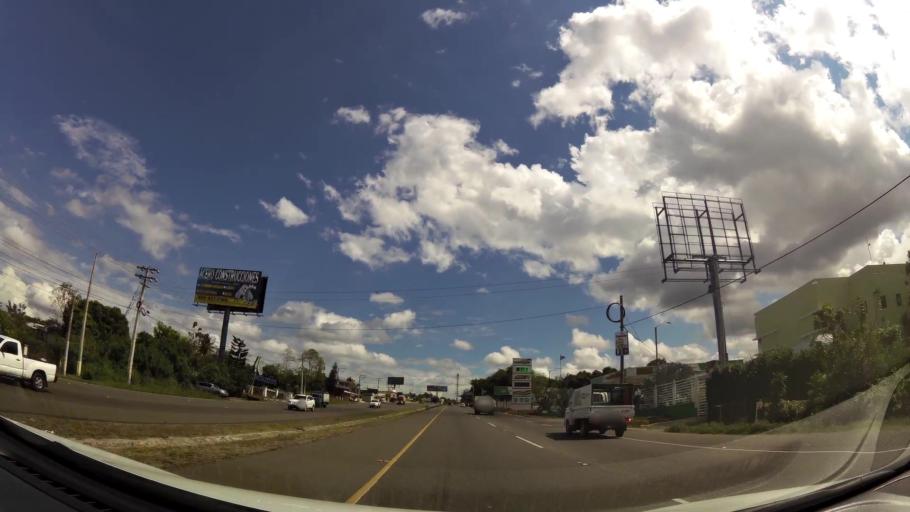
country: DO
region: Santiago
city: Licey al Medio
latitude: 19.3770
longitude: -70.6074
